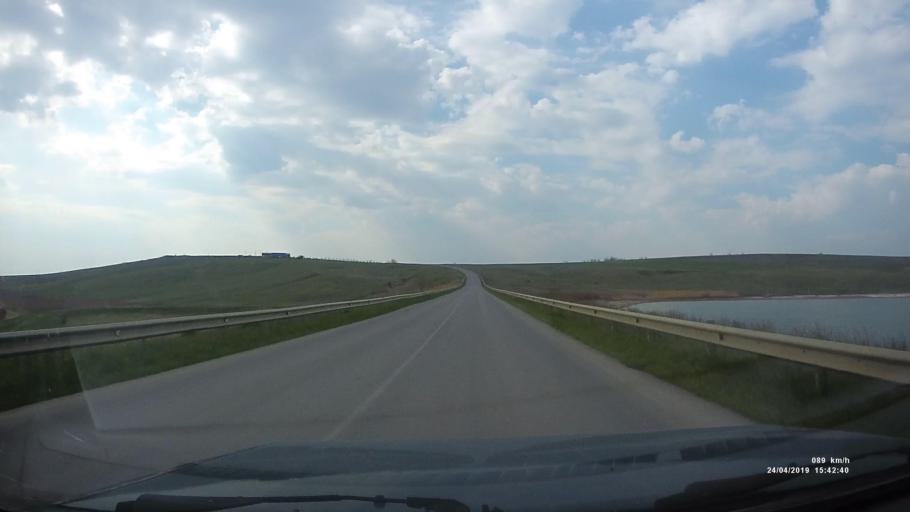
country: RU
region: Kalmykiya
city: Yashalta
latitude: 46.5779
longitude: 42.7850
